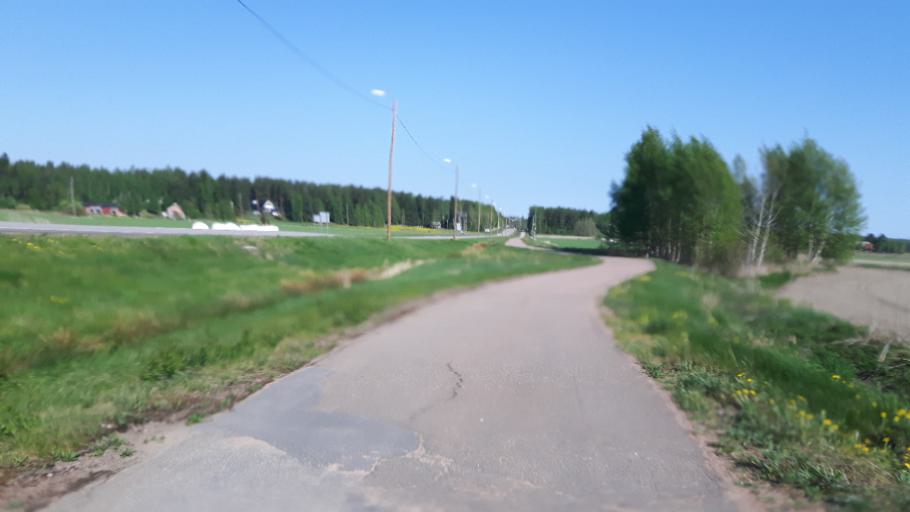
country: FI
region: Kymenlaakso
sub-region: Kotka-Hamina
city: Broby
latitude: 60.4963
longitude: 26.7959
